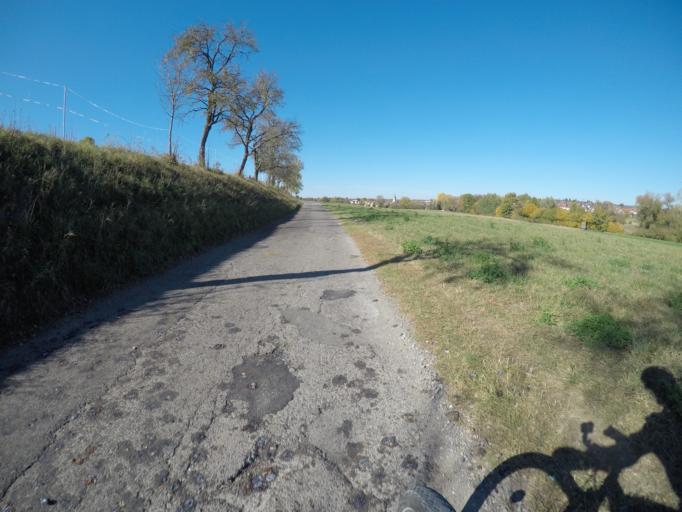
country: DE
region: Baden-Wuerttemberg
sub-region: Tuebingen Region
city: Rottenburg
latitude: 48.5297
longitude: 8.9547
